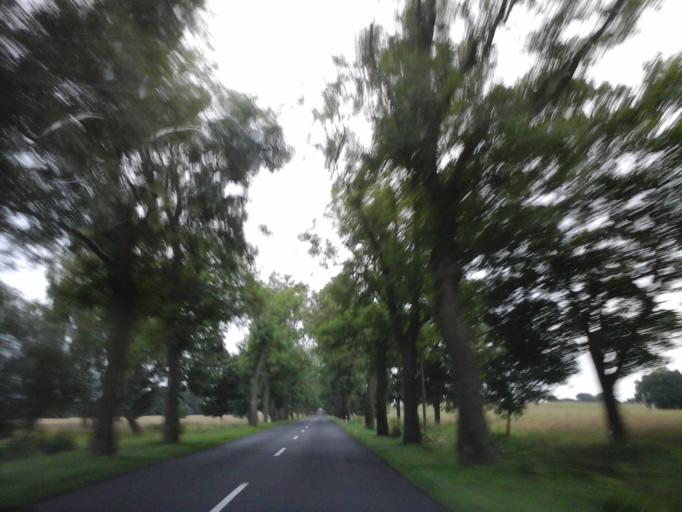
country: PL
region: West Pomeranian Voivodeship
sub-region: Powiat goleniowski
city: Maszewo
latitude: 53.5207
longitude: 15.1039
